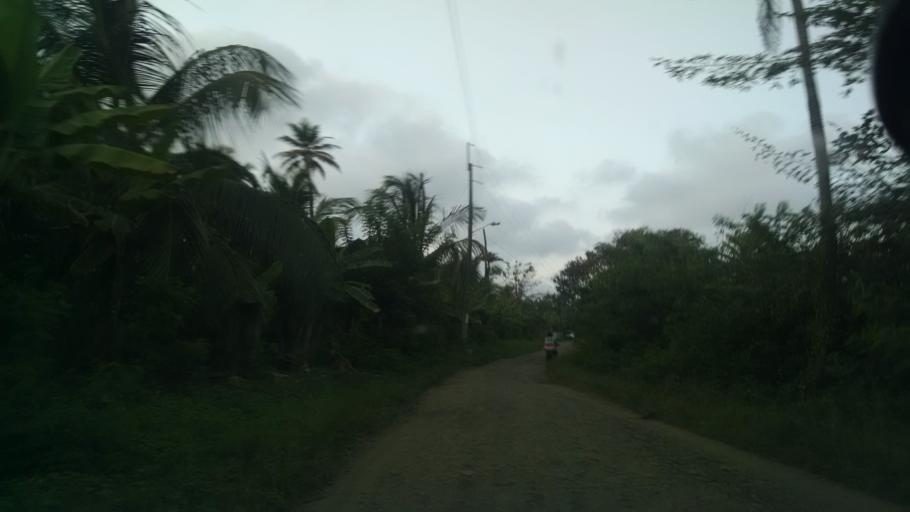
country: CO
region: Antioquia
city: San Juan de Uraba
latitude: 8.7352
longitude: -76.6068
